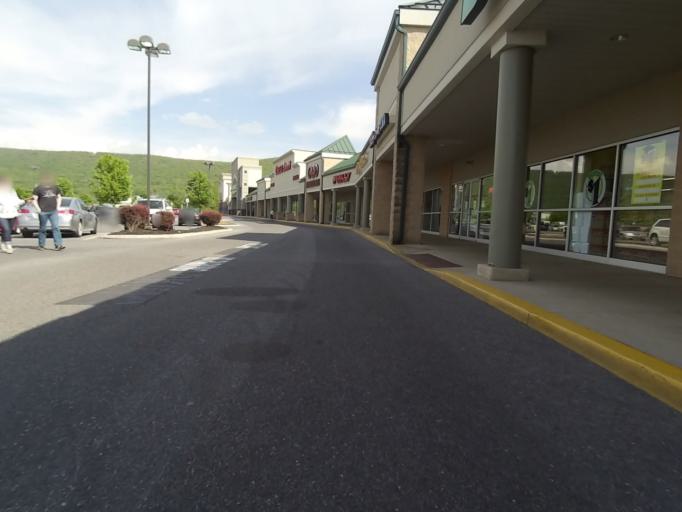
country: US
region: Pennsylvania
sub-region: Centre County
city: Houserville
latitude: 40.8313
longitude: -77.8090
